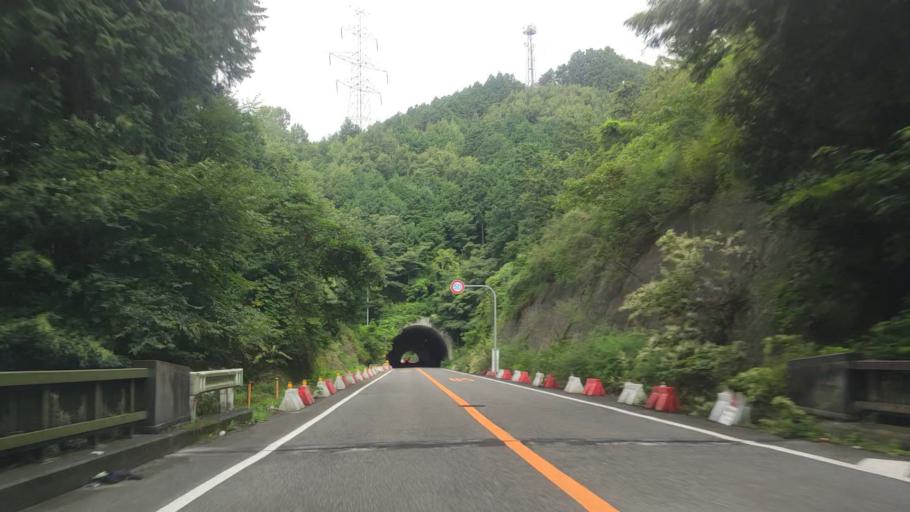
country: JP
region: Osaka
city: Tondabayashicho
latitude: 34.4187
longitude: 135.5865
